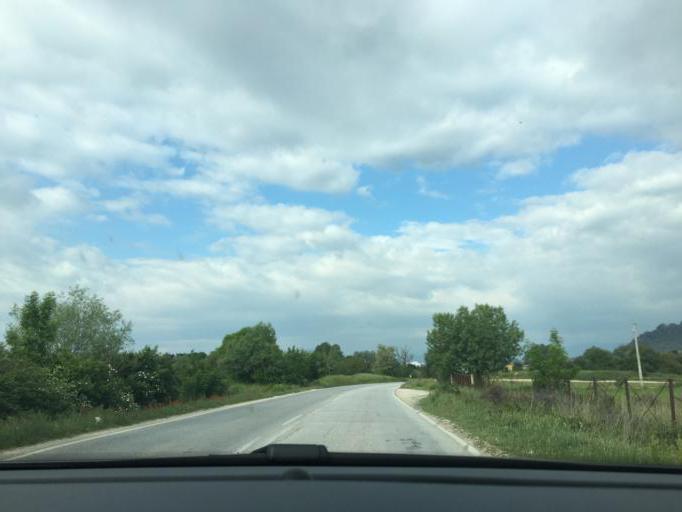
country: MK
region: Prilep
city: Prilep
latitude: 41.3598
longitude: 21.5915
